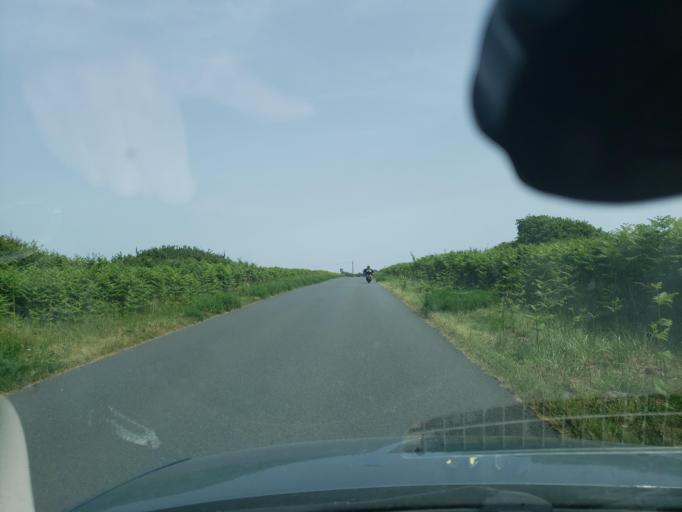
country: FR
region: Brittany
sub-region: Departement du Finistere
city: Guilvinec
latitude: 47.8038
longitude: -4.3062
